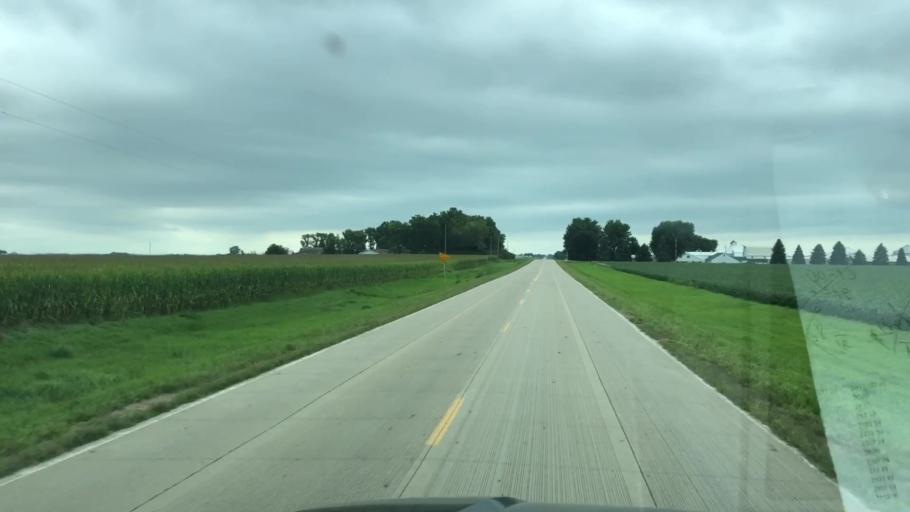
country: US
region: Iowa
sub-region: O'Brien County
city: Sheldon
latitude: 43.1451
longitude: -95.9795
